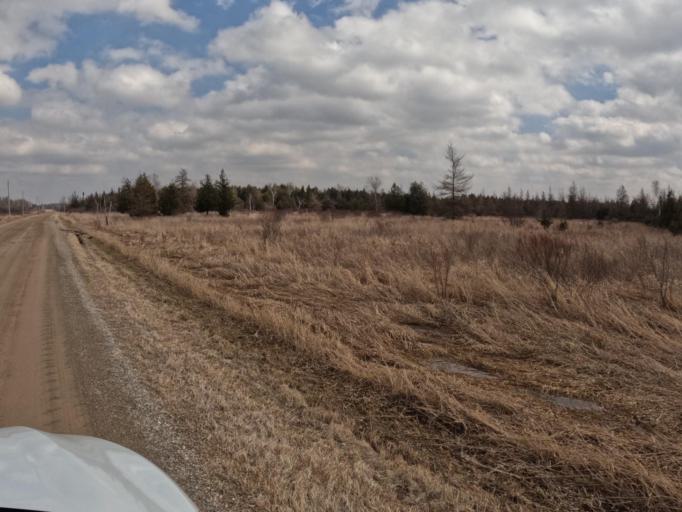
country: CA
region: Ontario
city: Shelburne
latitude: 44.0187
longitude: -80.3063
